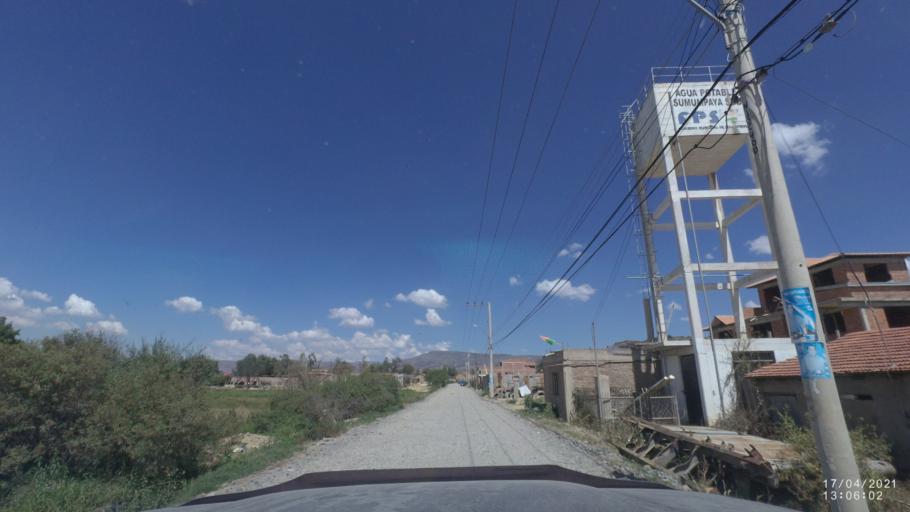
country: BO
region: Cochabamba
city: Cochabamba
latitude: -17.4079
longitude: -66.2246
